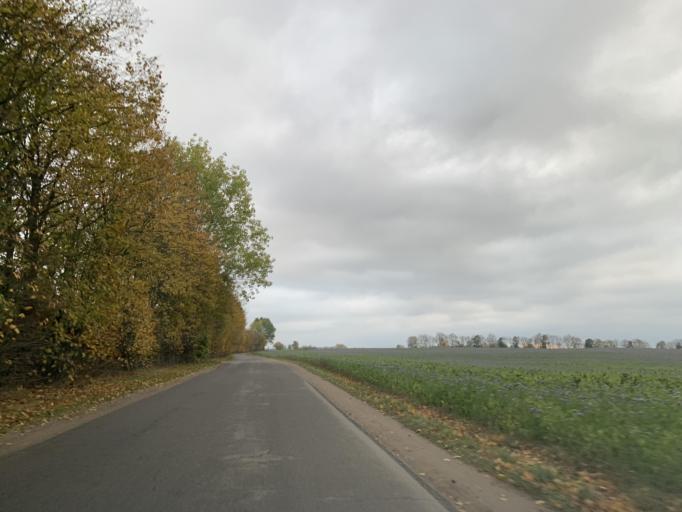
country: DE
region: Mecklenburg-Vorpommern
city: Gross Nemerow
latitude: 53.4771
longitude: 13.2660
